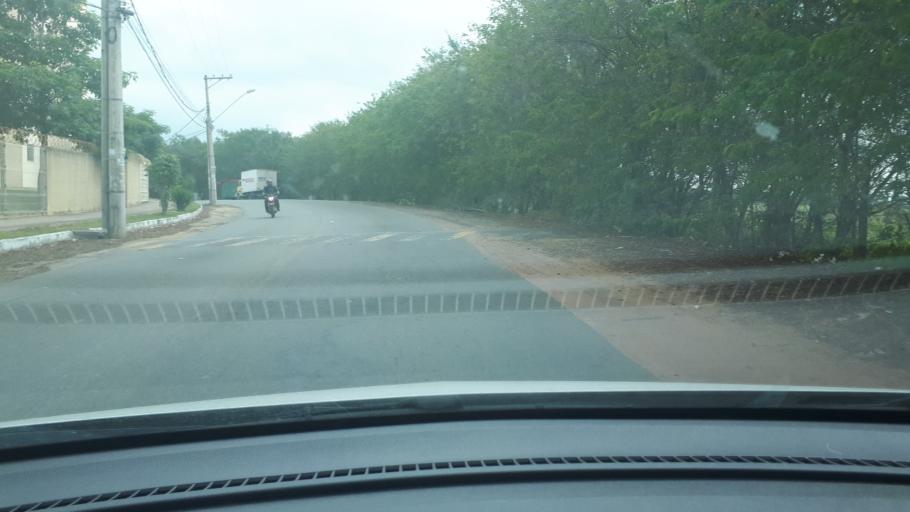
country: BR
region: Espirito Santo
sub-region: Serra
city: Serra
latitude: -20.1463
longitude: -40.1962
